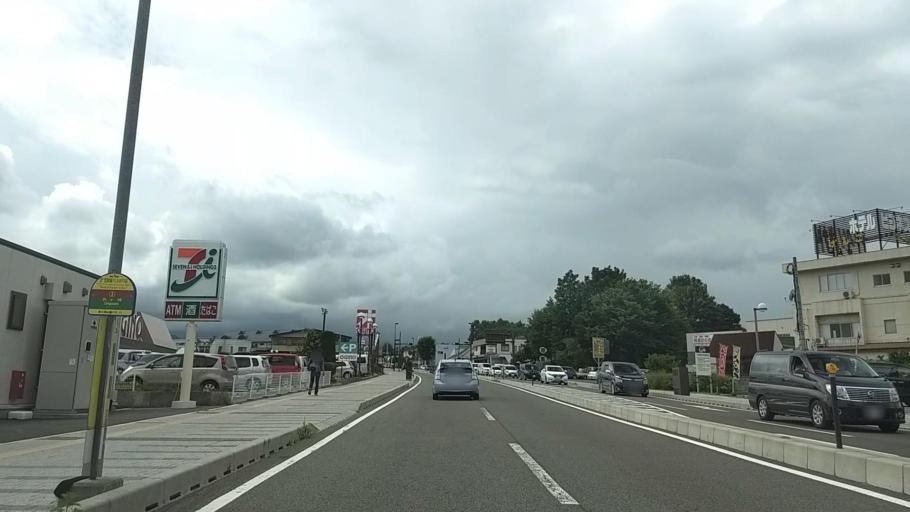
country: JP
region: Yamanashi
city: Fujikawaguchiko
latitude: 35.5028
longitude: 138.7574
